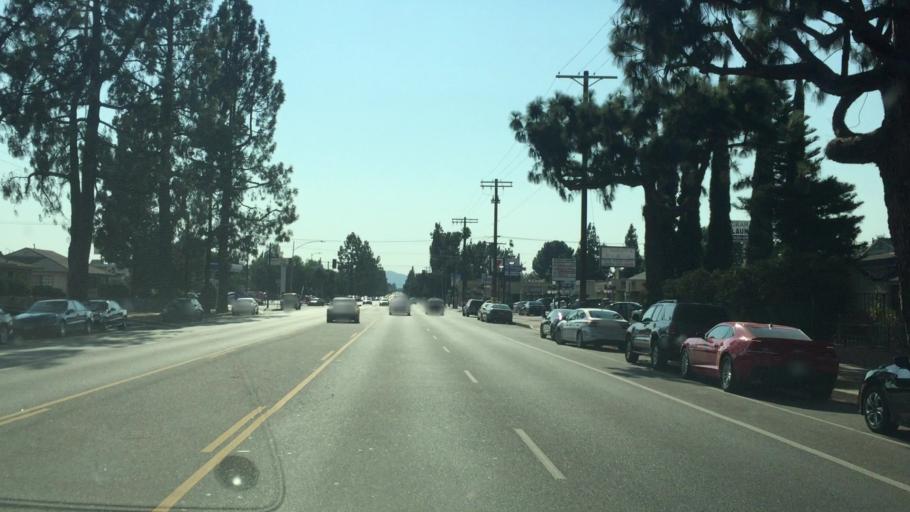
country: US
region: California
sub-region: Los Angeles County
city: San Fernando
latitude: 34.2572
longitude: -118.4833
